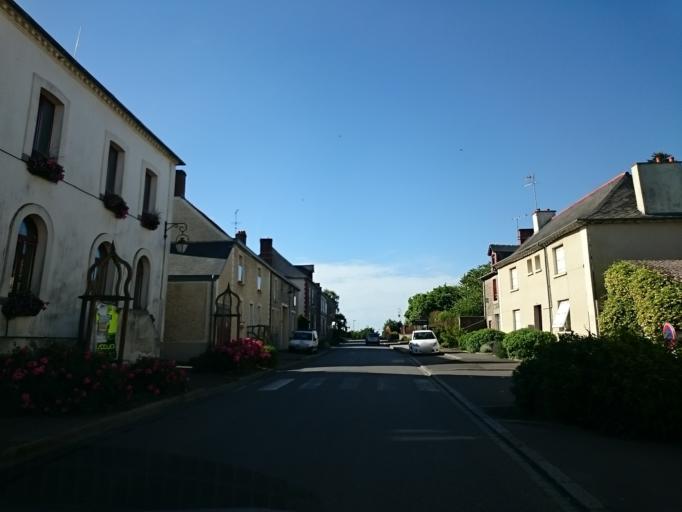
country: FR
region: Brittany
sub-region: Departement d'Ille-et-Vilaine
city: Corps-Nuds
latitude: 47.9790
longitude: -1.5878
